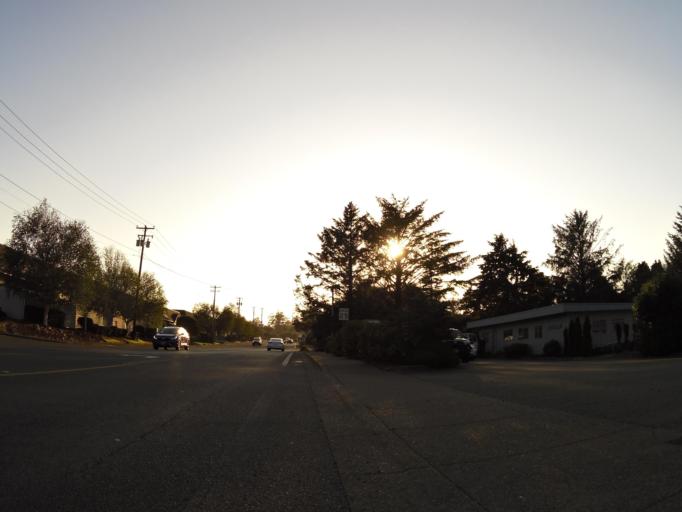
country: US
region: Oregon
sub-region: Lincoln County
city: Lincoln City
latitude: 44.9600
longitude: -124.0103
